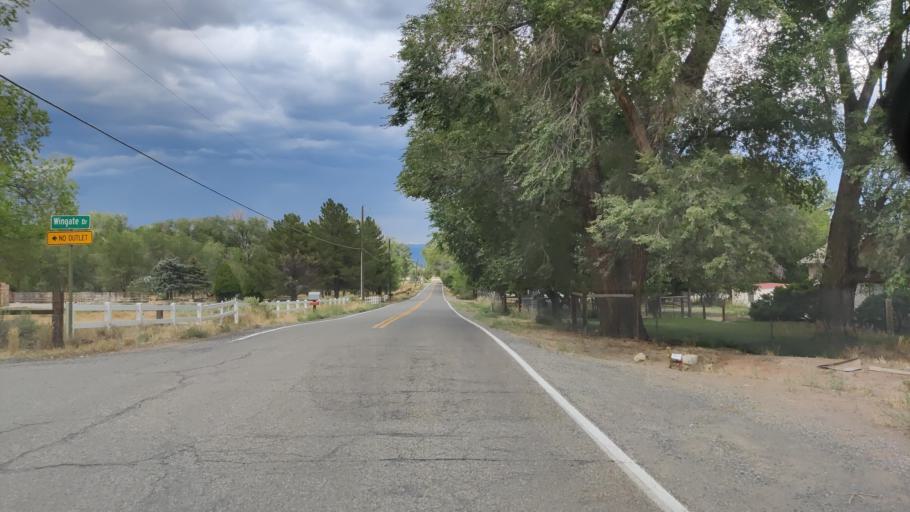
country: US
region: Colorado
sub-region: Mesa County
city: Redlands
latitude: 39.0951
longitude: -108.6920
